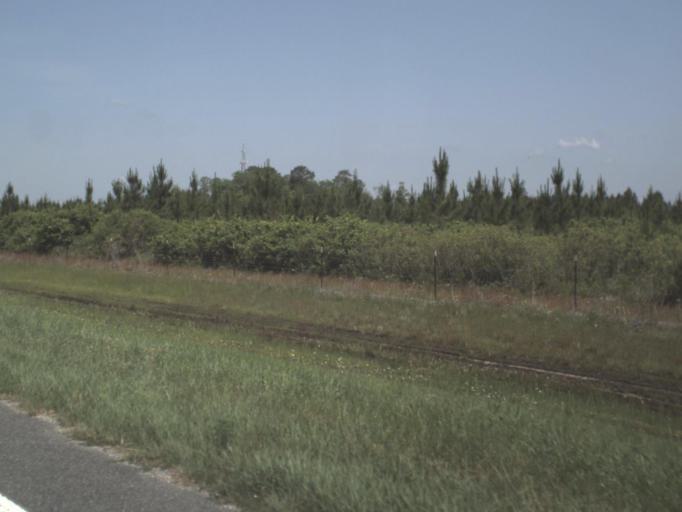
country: US
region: Florida
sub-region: Clay County
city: Middleburg
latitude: 29.9784
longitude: -81.8918
